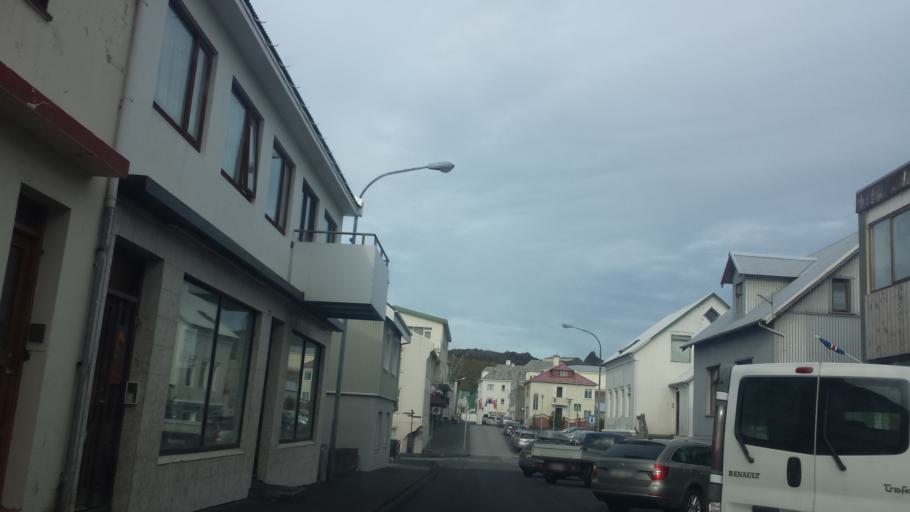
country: IS
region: South
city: Vestmannaeyjar
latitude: 63.4405
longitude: -20.2703
